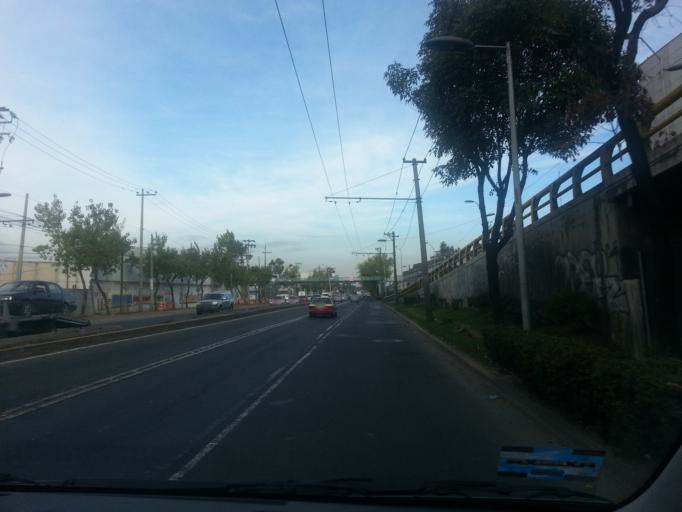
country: MX
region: Mexico City
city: Venustiano Carranza
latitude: 19.4217
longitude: -99.0833
